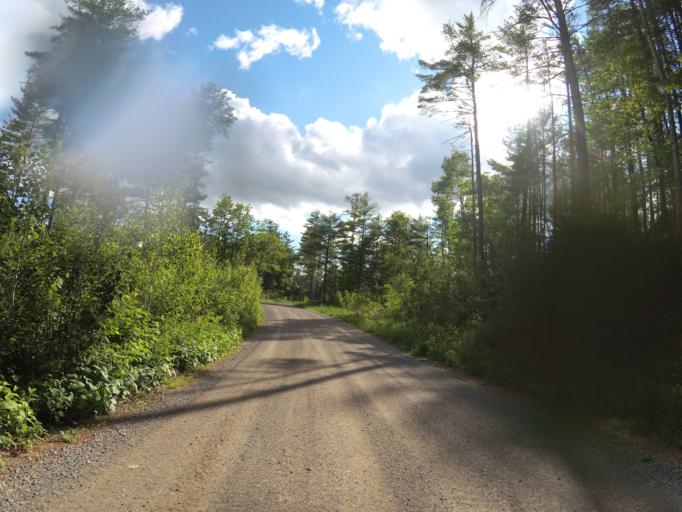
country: CA
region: Ontario
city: Renfrew
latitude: 45.1676
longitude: -76.9398
